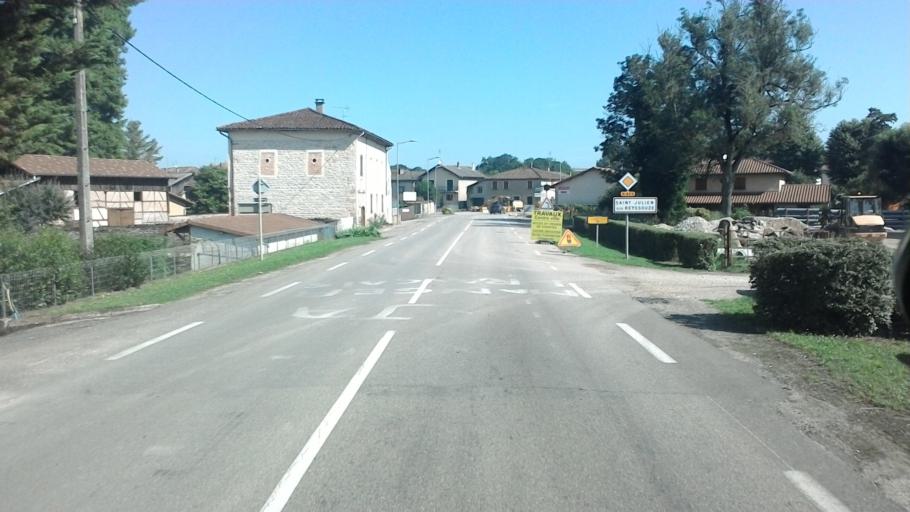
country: FR
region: Rhone-Alpes
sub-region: Departement de l'Ain
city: Montrevel-en-Bresse
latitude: 46.3993
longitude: 5.1134
